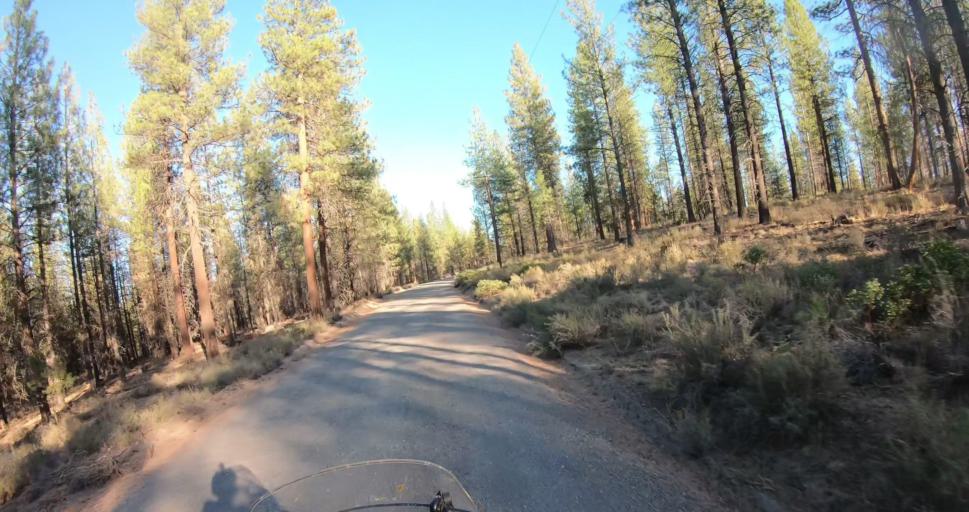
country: US
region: Oregon
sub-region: Deschutes County
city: La Pine
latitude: 43.7247
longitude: -121.4087
